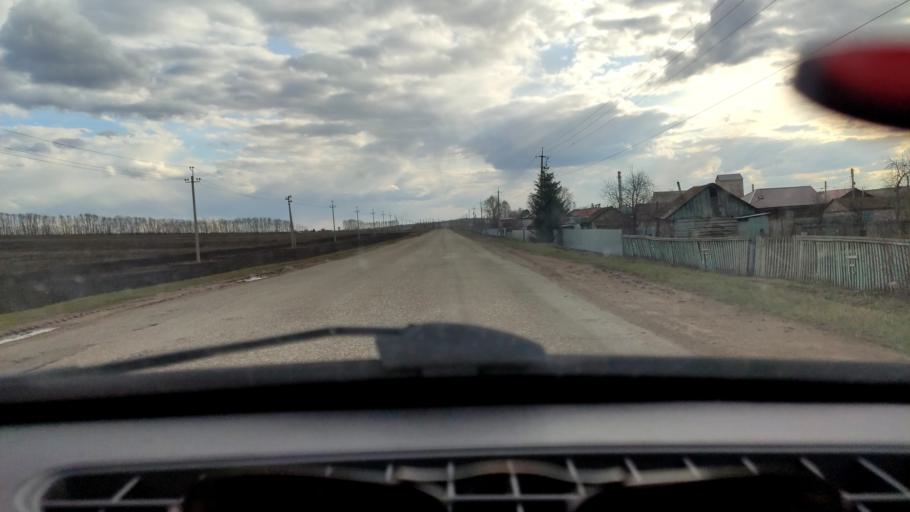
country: RU
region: Bashkortostan
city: Karmaskaly
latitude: 54.3984
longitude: 56.2470
